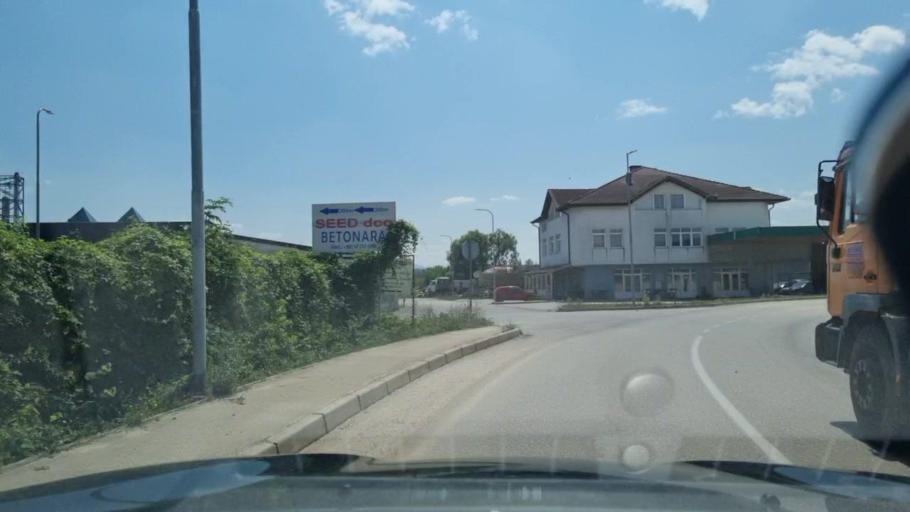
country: BA
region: Federation of Bosnia and Herzegovina
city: Sanski Most
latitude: 44.7476
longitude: 16.6768
